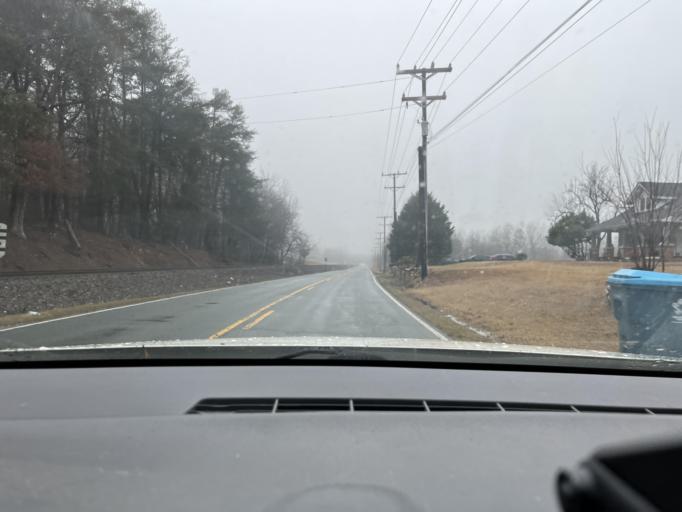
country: US
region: North Carolina
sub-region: Guilford County
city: Pleasant Garden
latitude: 35.9776
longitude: -79.7738
